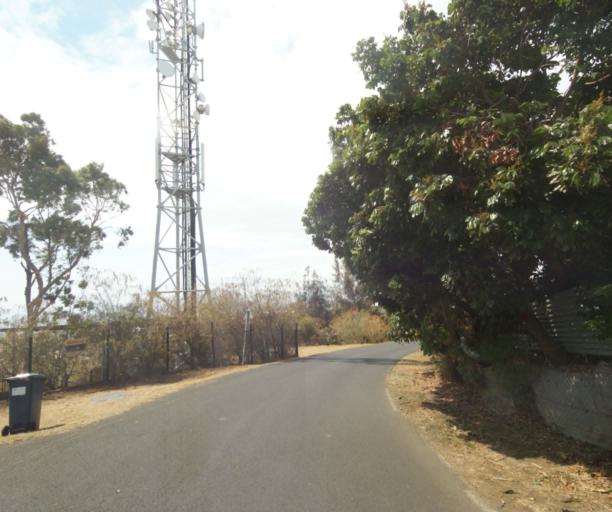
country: RE
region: Reunion
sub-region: Reunion
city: Saint-Paul
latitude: -21.0561
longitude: 55.2559
